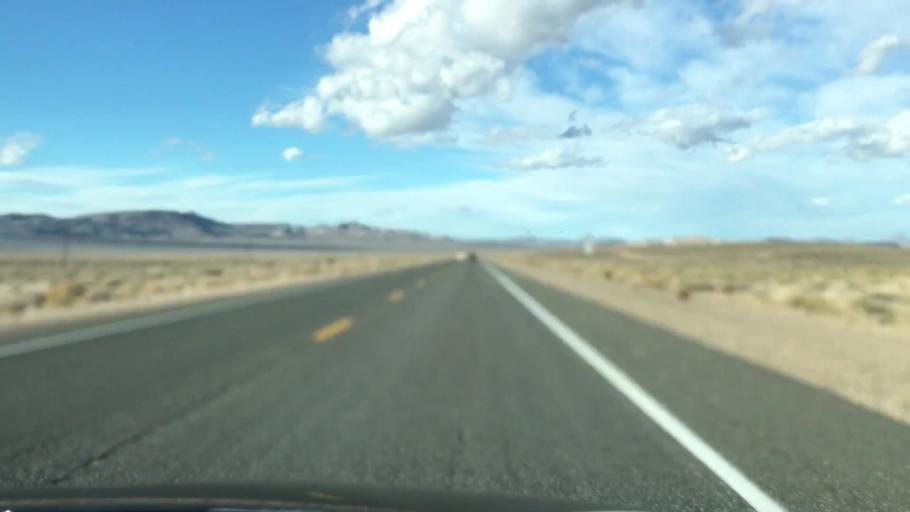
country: US
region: Nevada
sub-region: Esmeralda County
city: Goldfield
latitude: 37.4570
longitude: -117.1710
